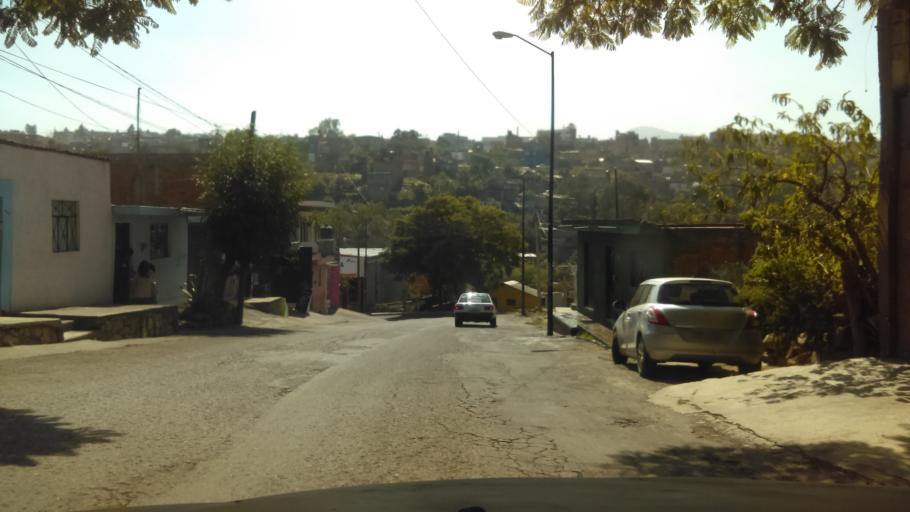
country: MX
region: Michoacan
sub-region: Morelia
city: Montana Monarca (Punta Altozano)
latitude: 19.6688
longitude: -101.1896
